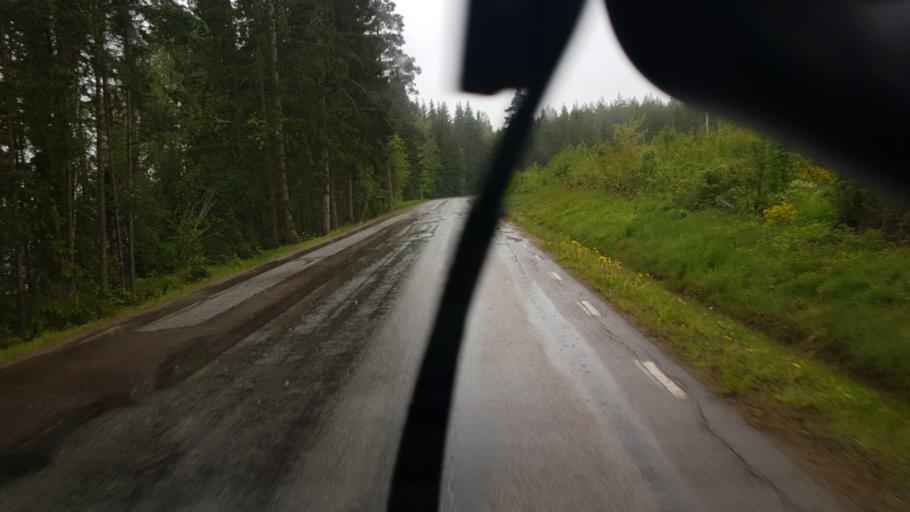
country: SE
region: Vaermland
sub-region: Arvika Kommun
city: Arvika
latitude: 59.7149
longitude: 12.5196
